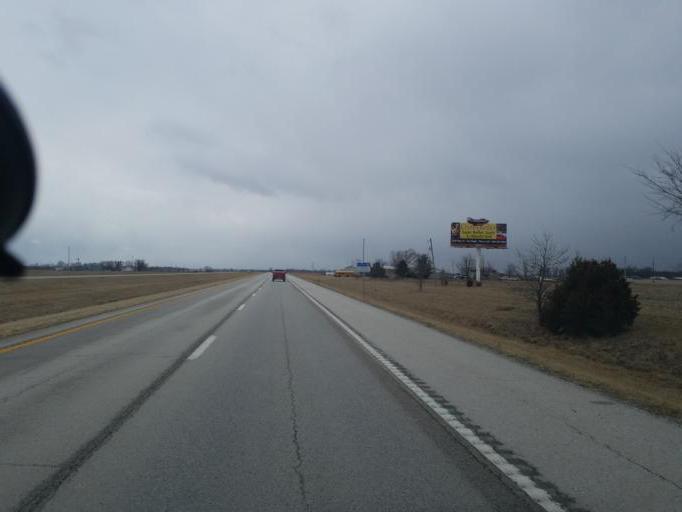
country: US
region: Missouri
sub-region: Randolph County
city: Moberly
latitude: 39.5035
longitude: -92.4353
